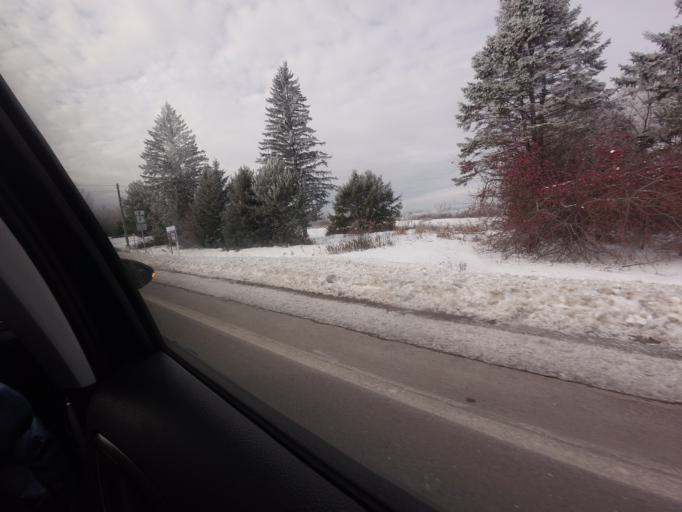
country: CA
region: New Brunswick
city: Oromocto
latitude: 45.8609
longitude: -66.4496
